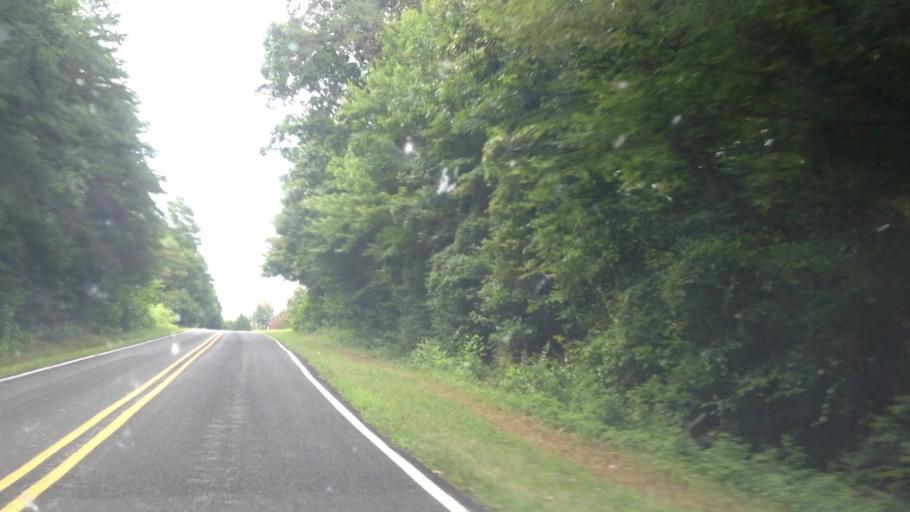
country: US
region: North Carolina
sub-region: Rockingham County
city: Mayodan
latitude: 36.4274
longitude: -80.0862
